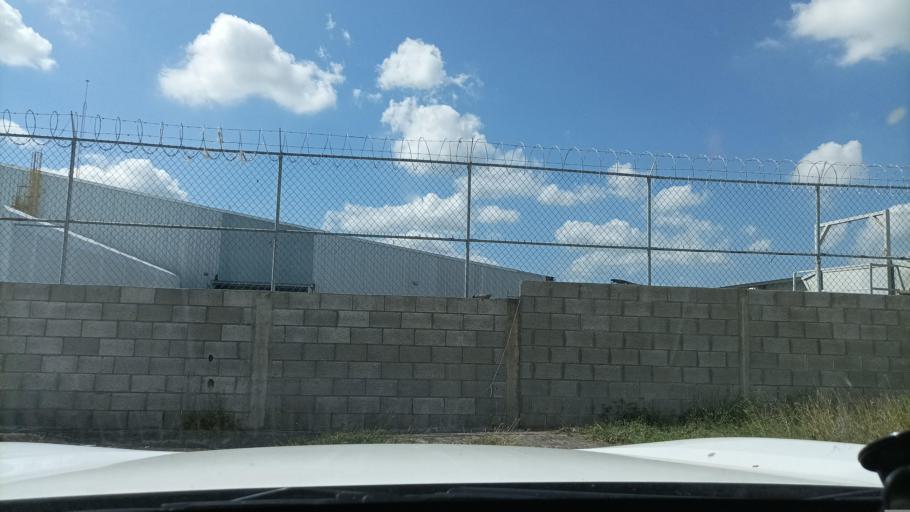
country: MX
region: Veracruz
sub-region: Veracruz
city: Las Amapolas
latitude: 19.1566
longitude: -96.2243
